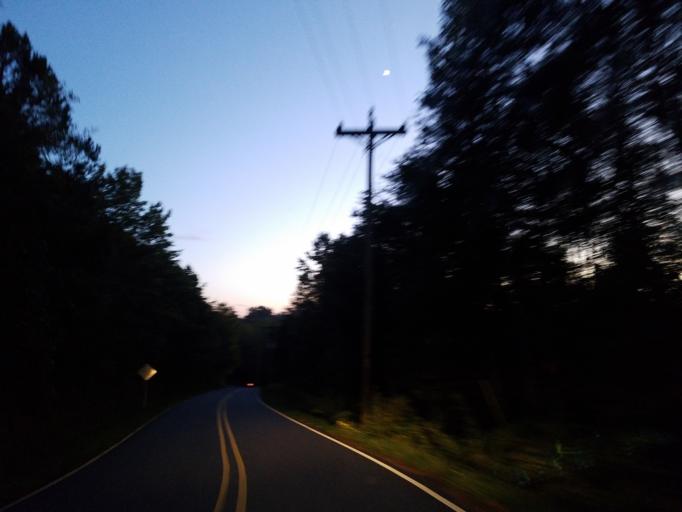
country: US
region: Georgia
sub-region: Dawson County
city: Dawsonville
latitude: 34.5210
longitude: -84.1831
